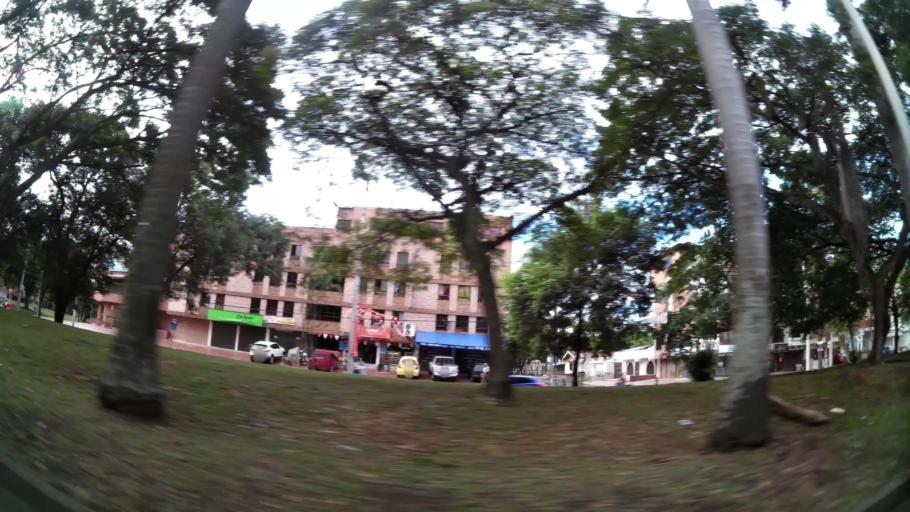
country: CO
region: Valle del Cauca
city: Cali
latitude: 3.4878
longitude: -76.5202
